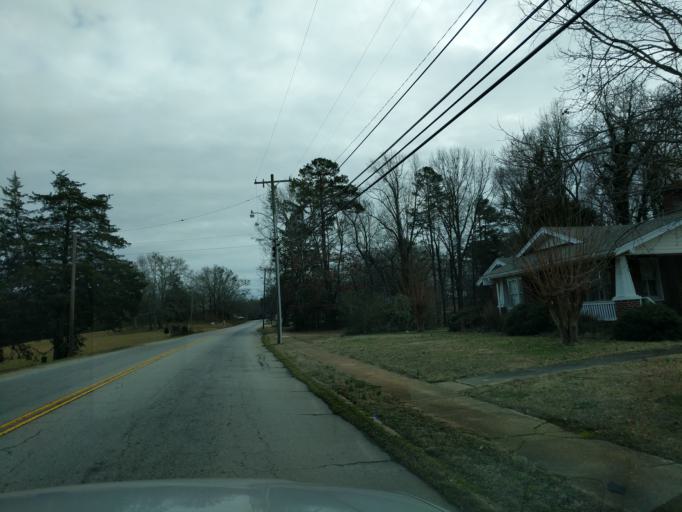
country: US
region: South Carolina
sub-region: Oconee County
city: Westminster
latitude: 34.6551
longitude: -83.0855
